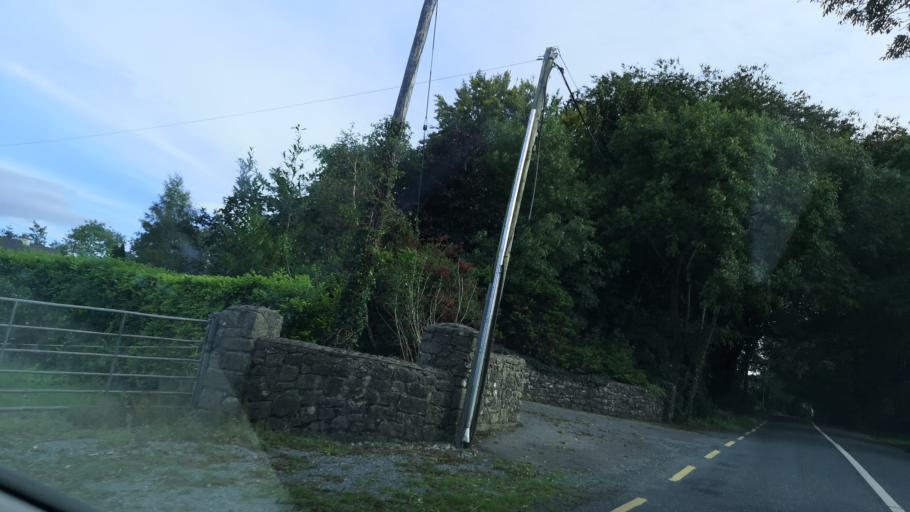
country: IE
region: Connaught
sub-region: County Galway
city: Ballinasloe
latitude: 53.3202
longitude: -8.2789
